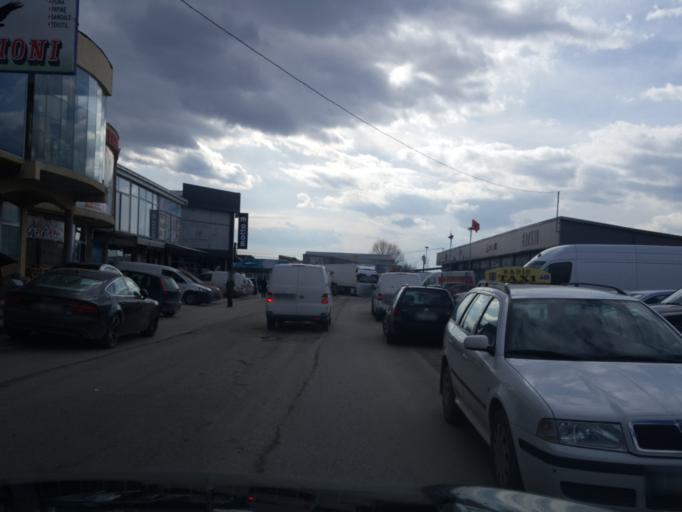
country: XK
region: Pristina
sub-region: Kosovo Polje
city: Kosovo Polje
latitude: 42.6439
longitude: 21.1286
